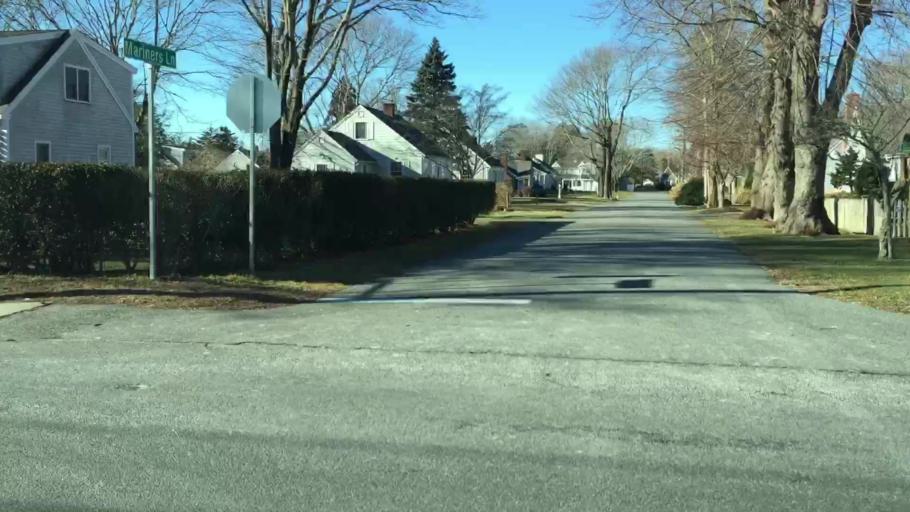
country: US
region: Massachusetts
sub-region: Barnstable County
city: Falmouth
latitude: 41.5458
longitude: -70.6150
